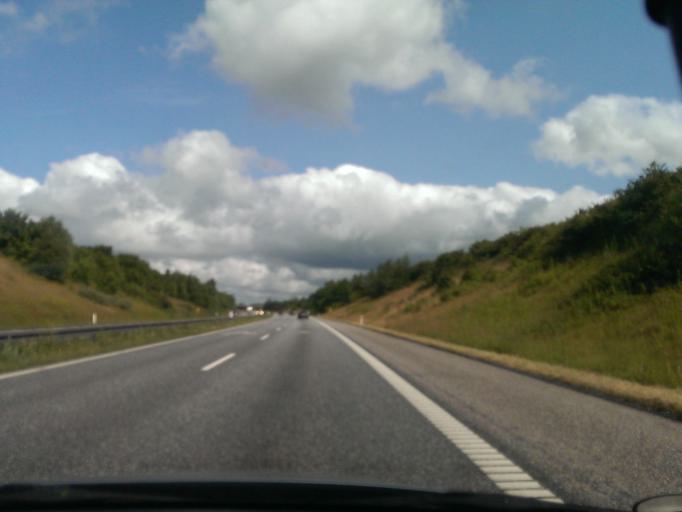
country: DK
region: North Denmark
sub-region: Mariagerfjord Kommune
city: Hobro
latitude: 56.7067
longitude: 9.7294
